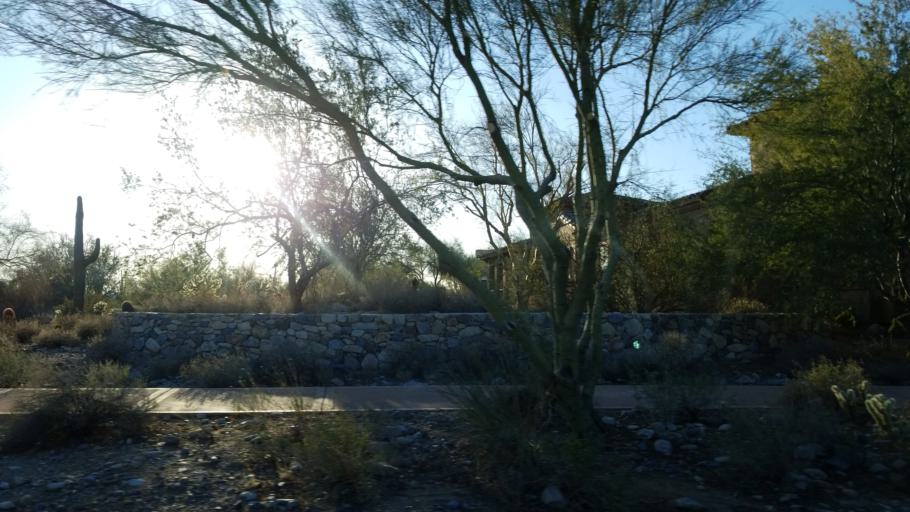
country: US
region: Arizona
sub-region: Maricopa County
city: Paradise Valley
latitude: 33.6441
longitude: -111.8785
